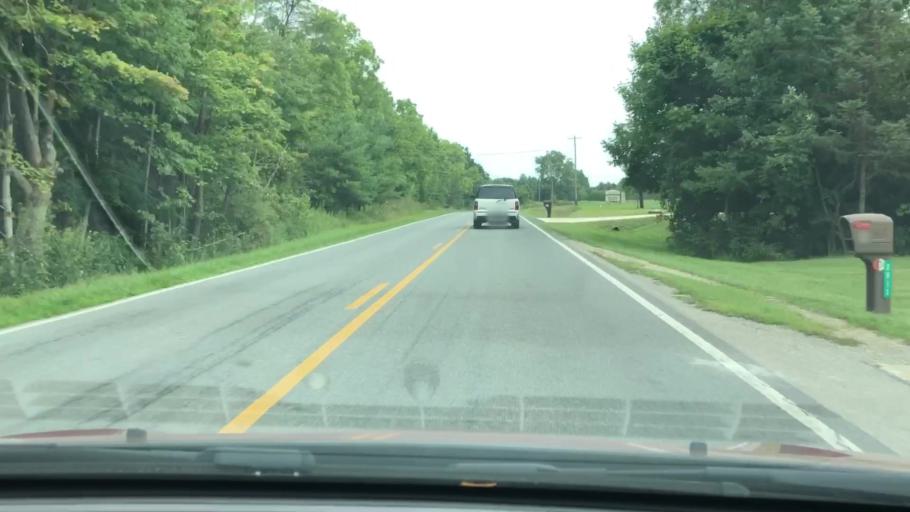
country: US
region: Ohio
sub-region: Delaware County
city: Sunbury
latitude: 40.2102
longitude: -82.8724
